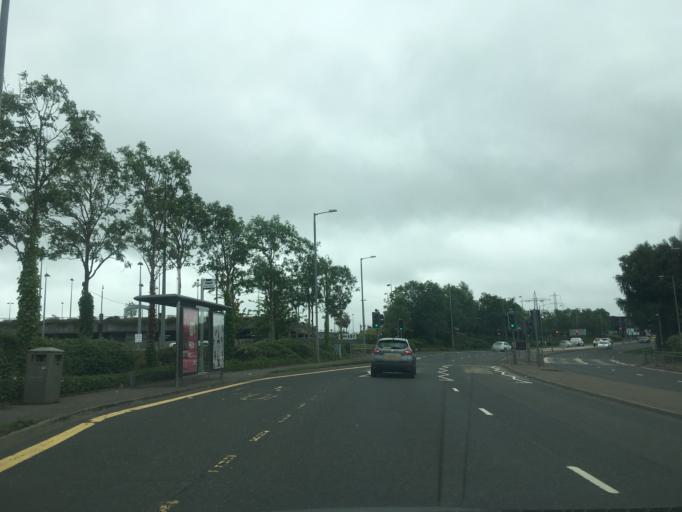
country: GB
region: Scotland
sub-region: Renfrewshire
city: Renfrew
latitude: 55.8761
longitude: -4.3689
